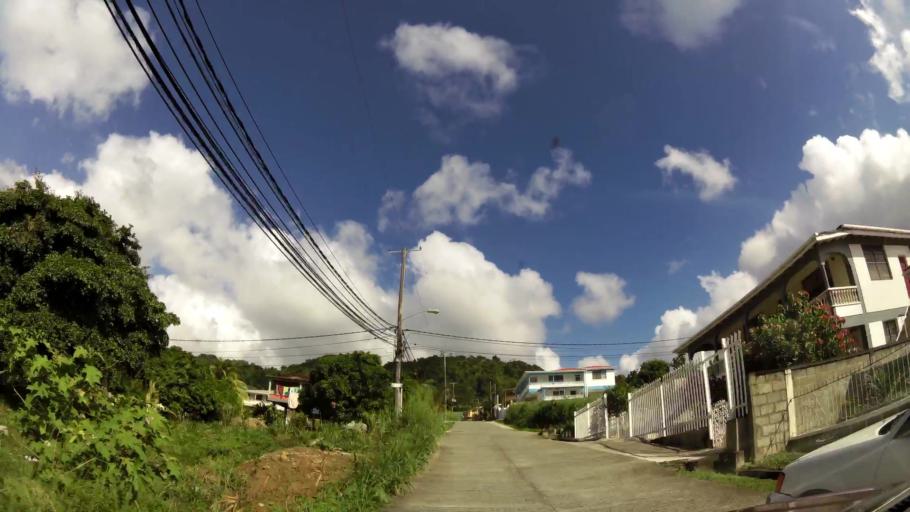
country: DM
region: Saint Luke
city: Pointe Michel
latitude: 15.2811
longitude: -61.3726
